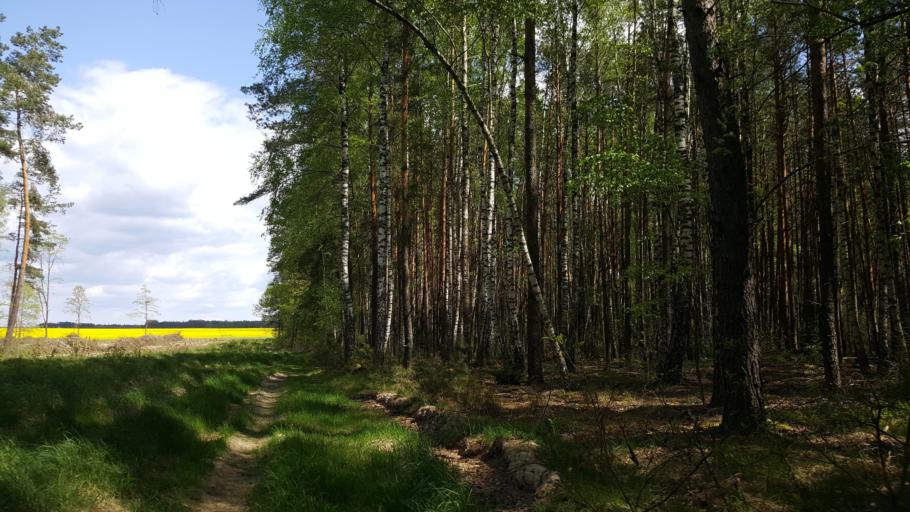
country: BY
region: Brest
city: Kamyanyets
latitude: 52.3870
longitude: 23.9337
